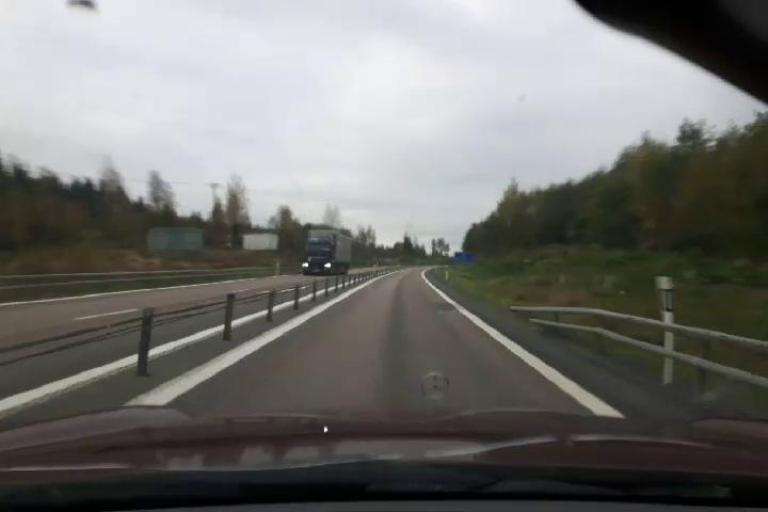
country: SE
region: Vaesternorrland
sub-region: Kramfors Kommun
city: Nordingra
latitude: 62.9190
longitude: 18.0984
